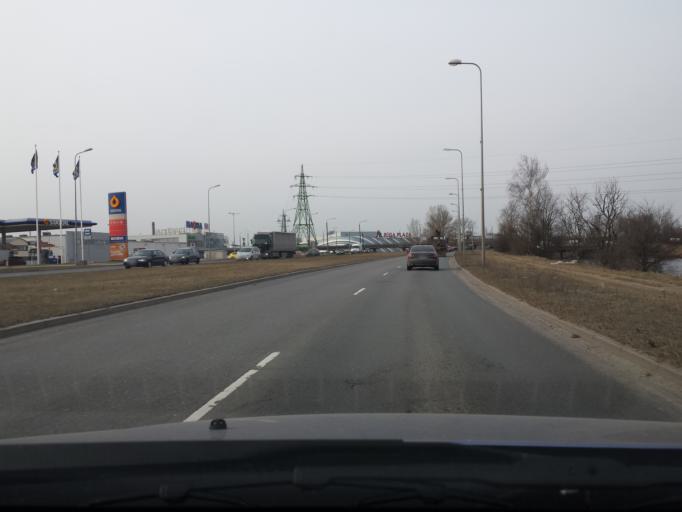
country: LV
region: Riga
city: Riga
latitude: 56.9215
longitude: 24.1096
